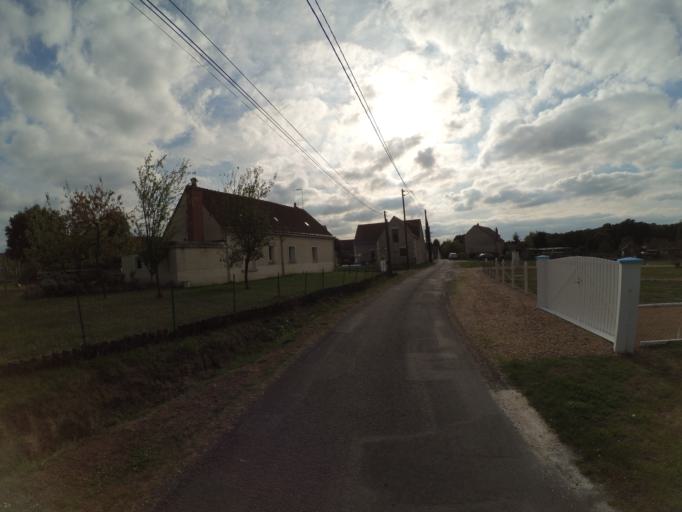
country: FR
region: Centre
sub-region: Departement d'Indre-et-Loire
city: Poce-sur-Cisse
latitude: 47.4729
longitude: 0.9665
